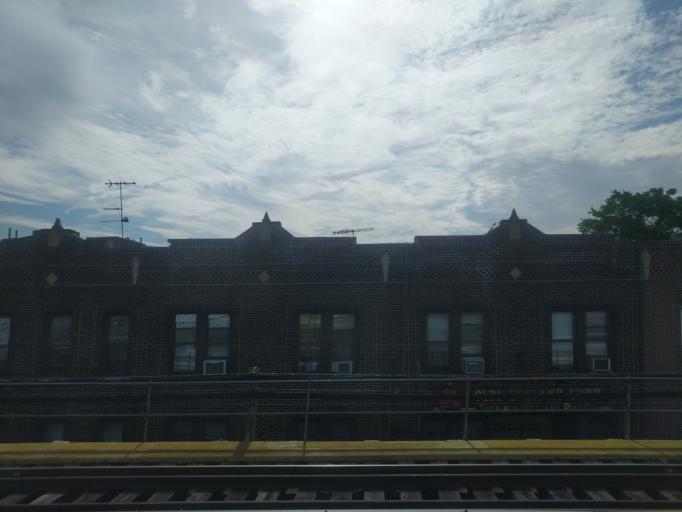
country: US
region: New York
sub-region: Kings County
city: Bensonhurst
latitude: 40.6376
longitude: -73.9946
